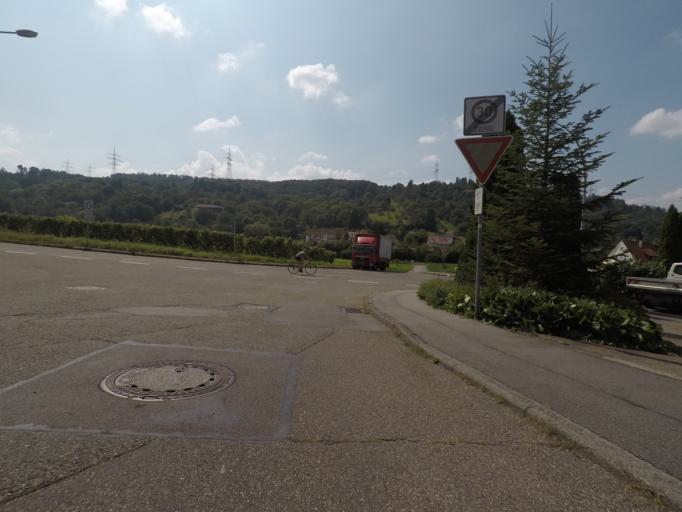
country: DE
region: Baden-Wuerttemberg
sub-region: Regierungsbezirk Stuttgart
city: Weinstadt-Endersbach
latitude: 48.7869
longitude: 9.4086
